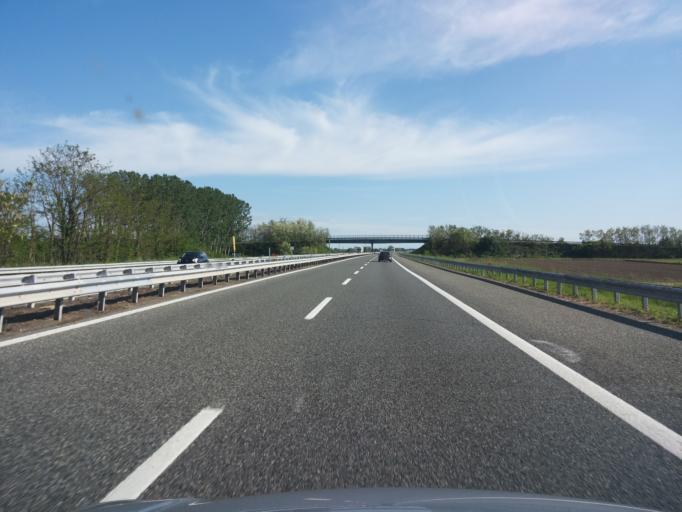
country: IT
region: Piedmont
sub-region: Provincia di Novara
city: Landiona
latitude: 45.4989
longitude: 8.4382
